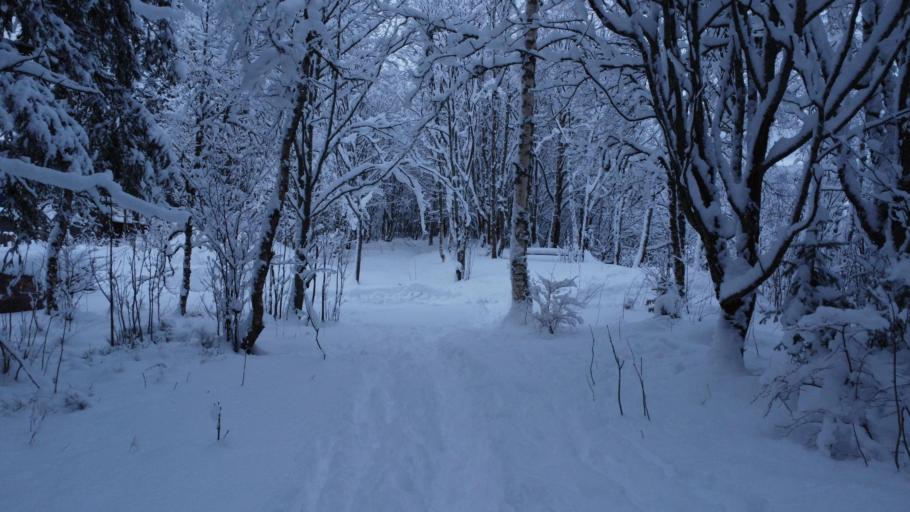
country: NO
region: Nordland
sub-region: Rana
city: Mo i Rana
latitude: 66.3355
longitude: 14.1509
